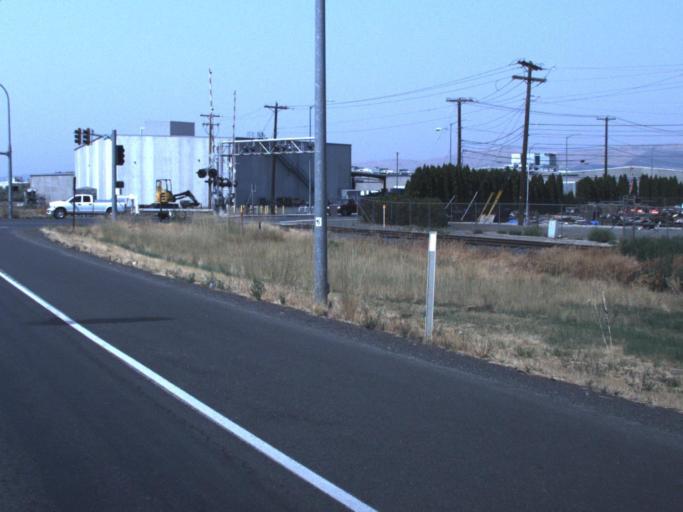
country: US
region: Washington
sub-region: Yakima County
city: Terrace Heights
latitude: 46.5620
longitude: -120.4031
